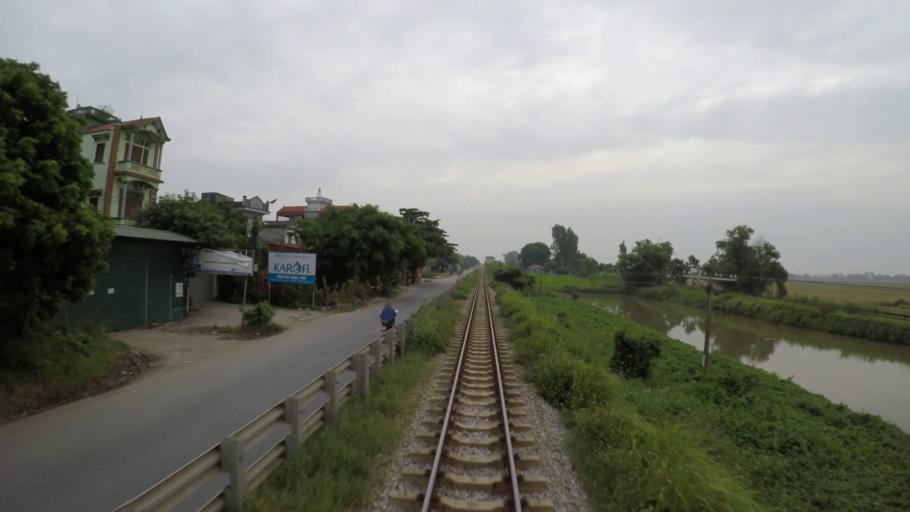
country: VN
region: Hung Yen
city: Ban Yen Nhan
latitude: 20.9683
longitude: 106.1054
